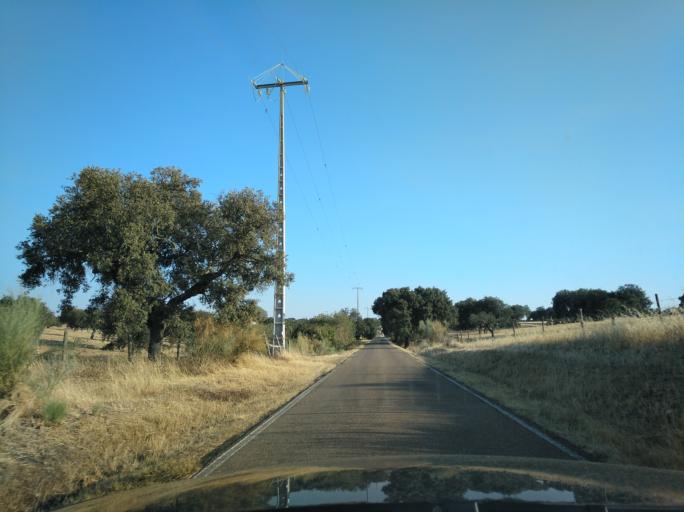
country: PT
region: Portalegre
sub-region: Campo Maior
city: Campo Maior
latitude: 39.0826
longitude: -7.1172
